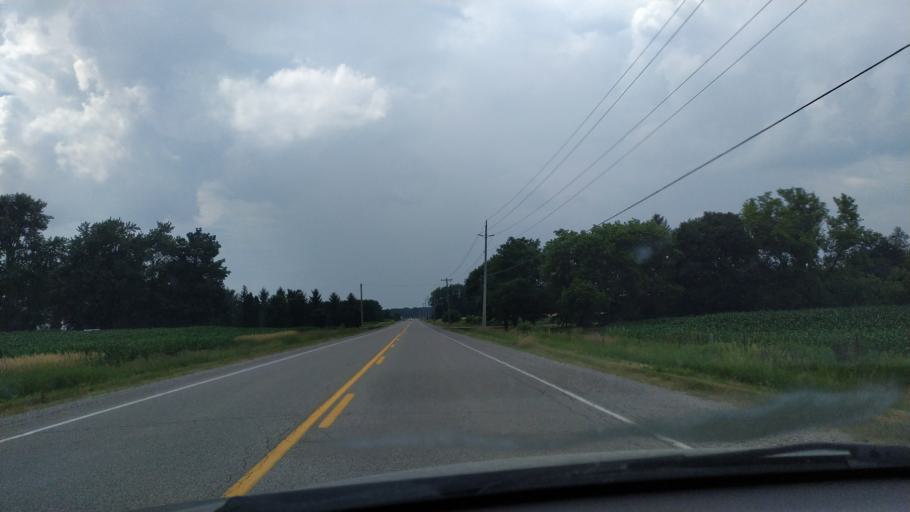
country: CA
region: Ontario
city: London
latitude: 43.2149
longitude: -81.1601
